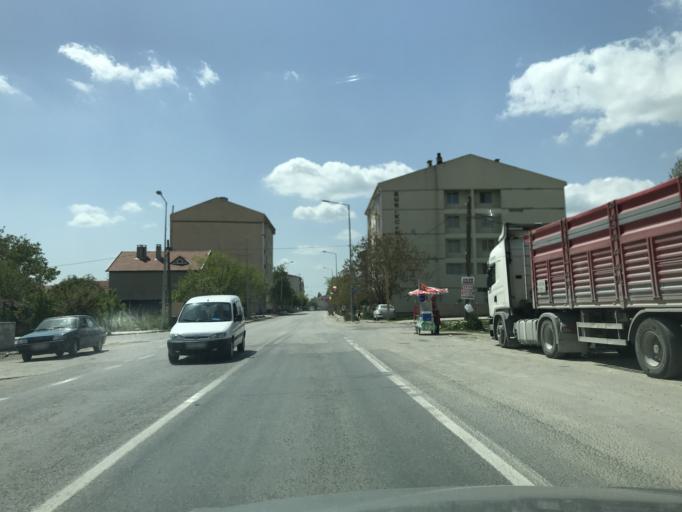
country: TR
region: Kirklareli
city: Pinarhisar
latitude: 41.6223
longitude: 27.5283
